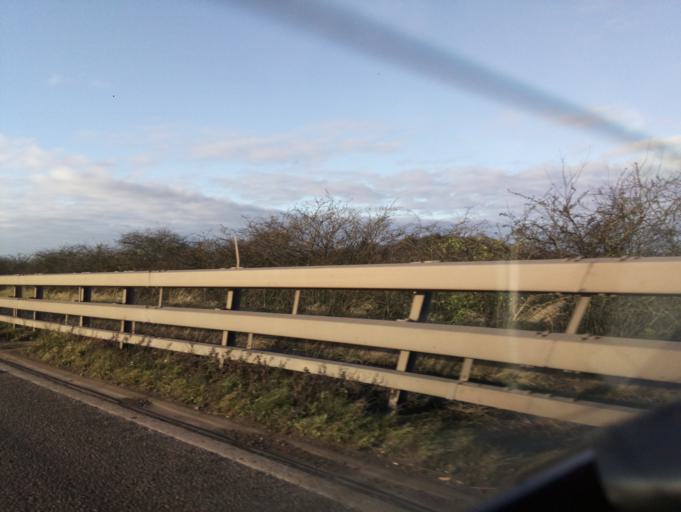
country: GB
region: England
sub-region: Derbyshire
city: Etwall
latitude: 52.8525
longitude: -1.5857
